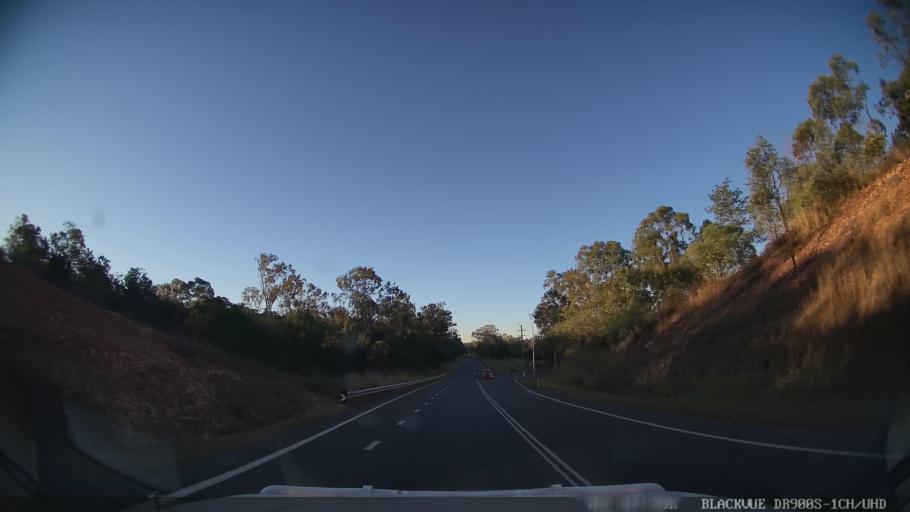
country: AU
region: Queensland
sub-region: Gladstone
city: Toolooa
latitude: -23.9621
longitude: 151.2179
